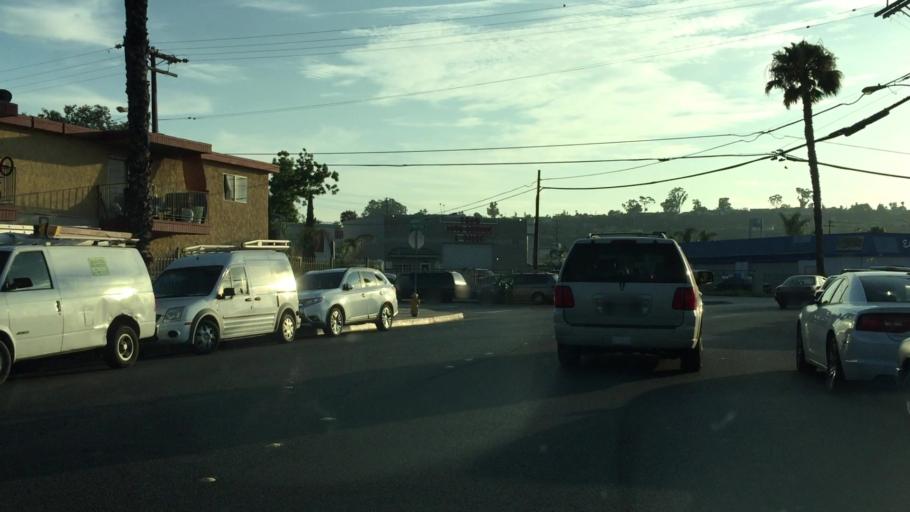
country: US
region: California
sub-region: San Diego County
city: El Cajon
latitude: 32.7924
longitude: -116.9685
